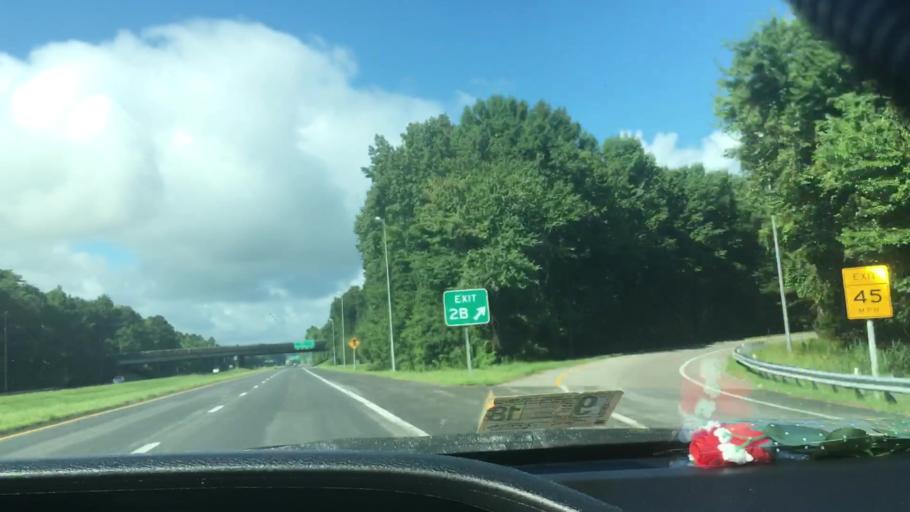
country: US
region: Virginia
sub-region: City of Portsmouth
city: Portsmouth Heights
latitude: 36.8011
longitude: -76.3752
